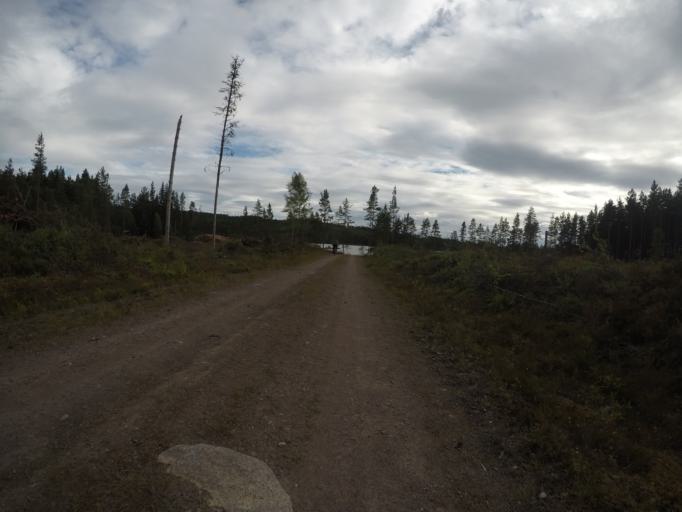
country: SE
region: Vaermland
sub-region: Filipstads Kommun
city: Lesjofors
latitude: 60.0136
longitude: 14.3971
